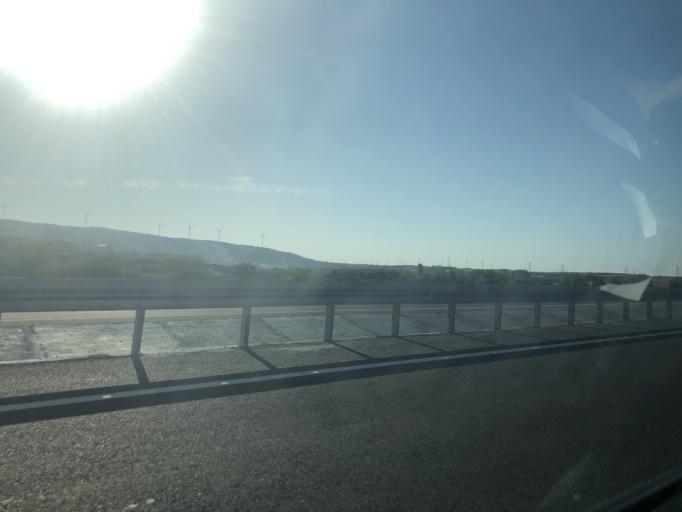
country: TR
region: Istanbul
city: Catalca
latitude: 41.1612
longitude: 28.4628
